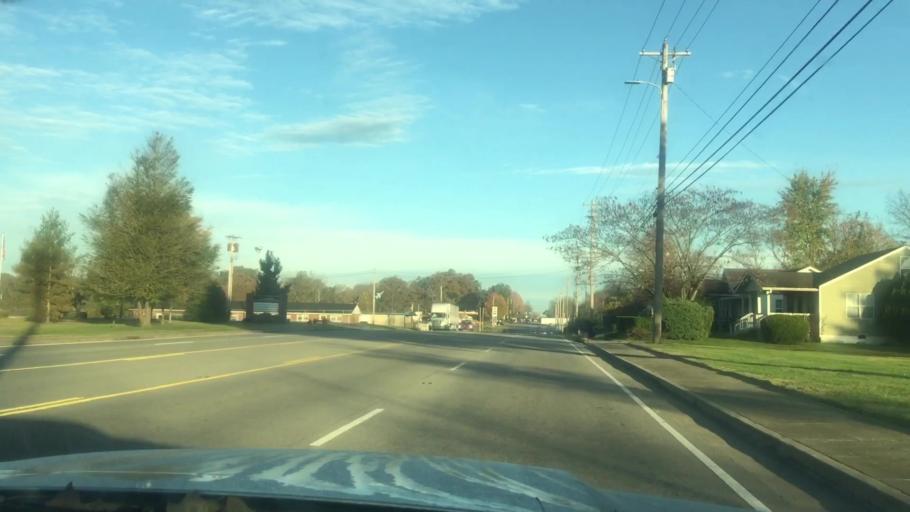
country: US
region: Tennessee
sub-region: Coffee County
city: Tullahoma
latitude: 35.3525
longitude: -86.2030
